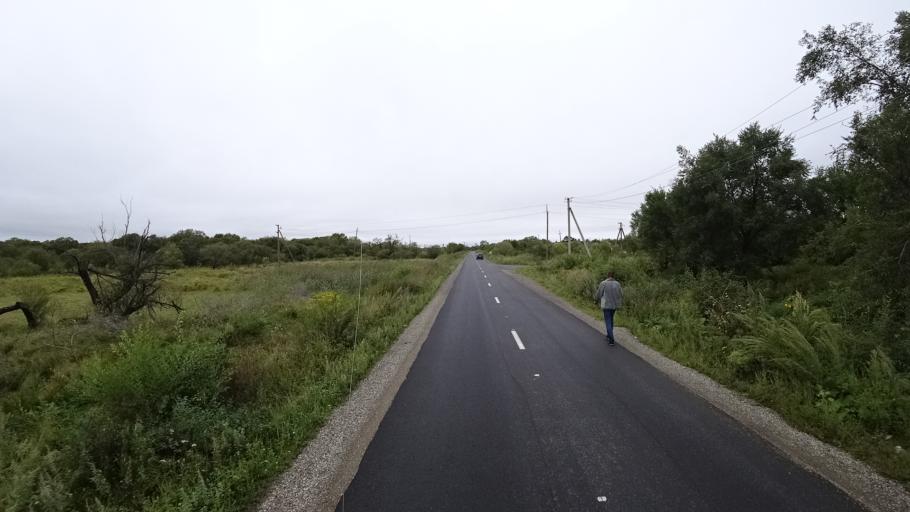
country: RU
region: Primorskiy
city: Monastyrishche
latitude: 44.1999
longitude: 132.4462
